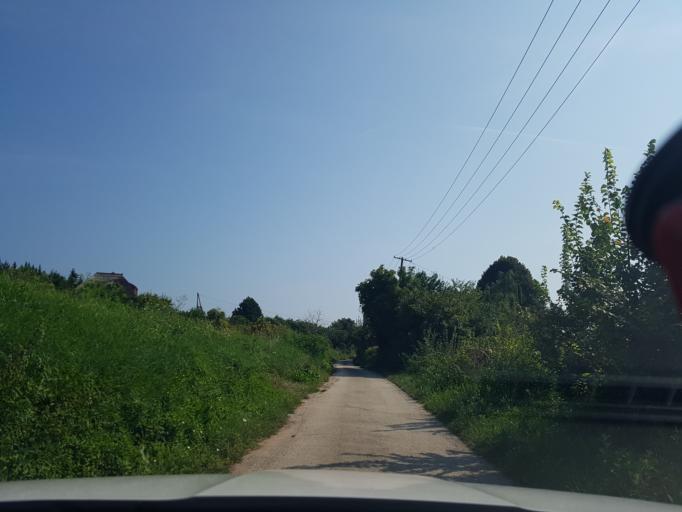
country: HU
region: Veszprem
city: Balatonalmadi
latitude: 47.0005
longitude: 17.9865
